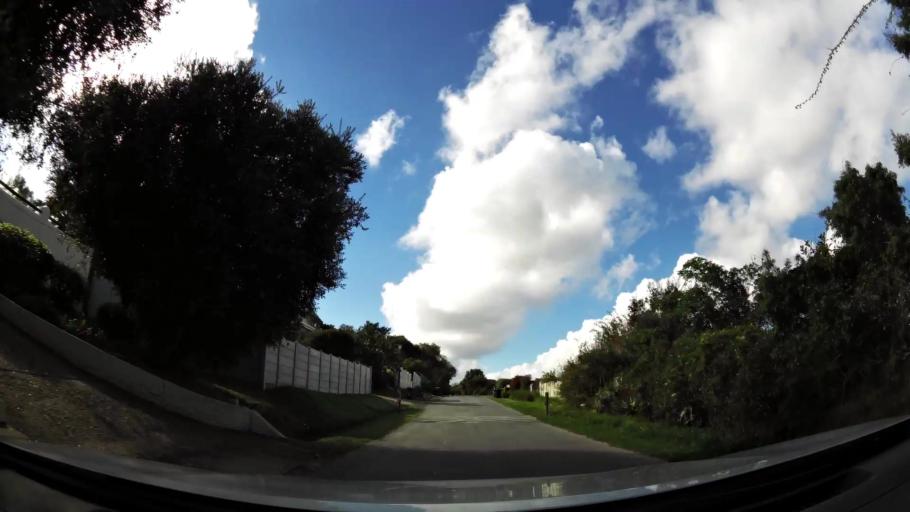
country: ZA
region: Western Cape
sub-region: Eden District Municipality
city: Knysna
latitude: -34.0376
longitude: 23.0691
